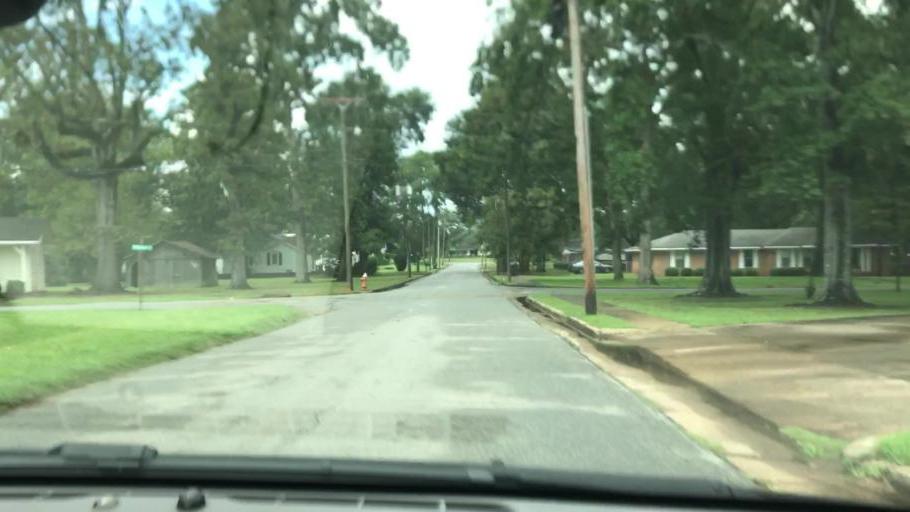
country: US
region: Georgia
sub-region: Early County
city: Blakely
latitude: 31.3733
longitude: -84.9469
